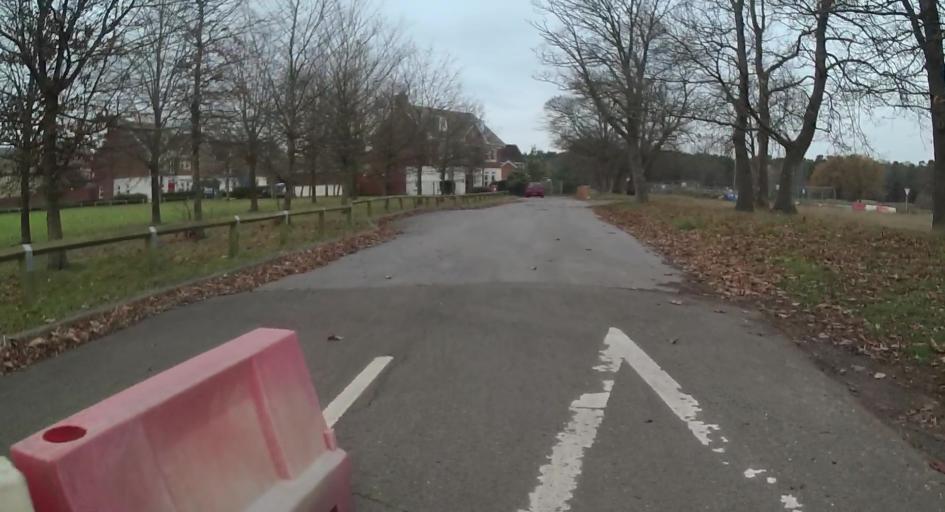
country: GB
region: England
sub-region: Surrey
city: Bagshot
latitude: 51.3145
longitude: -0.6950
